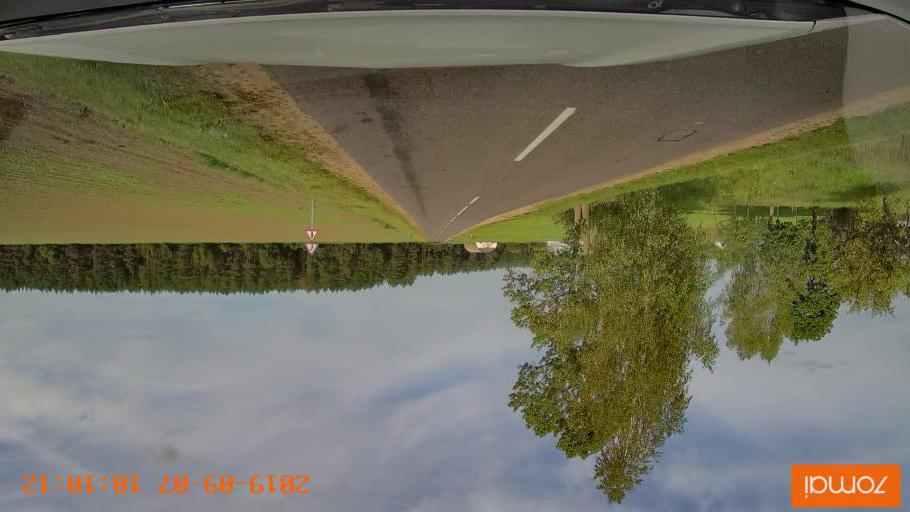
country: BY
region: Grodnenskaya
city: Voranava
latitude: 54.1056
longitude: 25.3711
